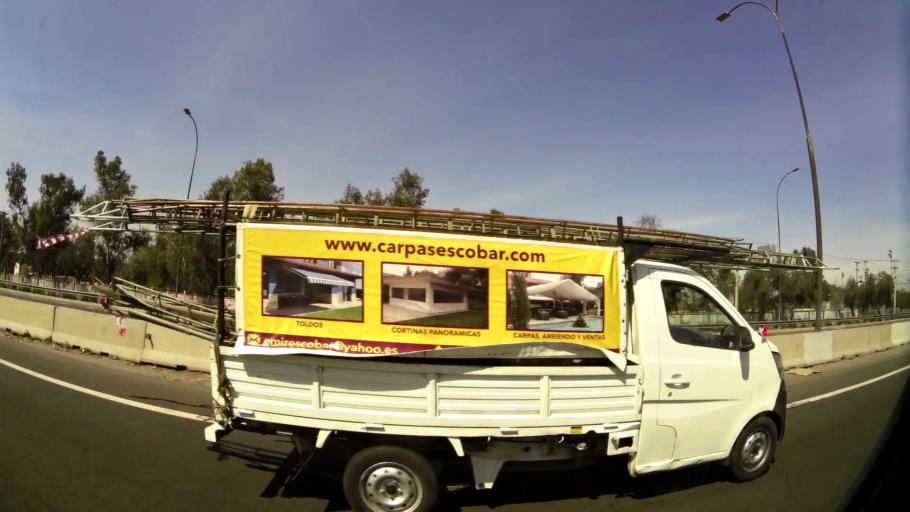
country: CL
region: Santiago Metropolitan
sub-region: Provincia de Santiago
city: Santiago
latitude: -33.5184
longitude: -70.6748
